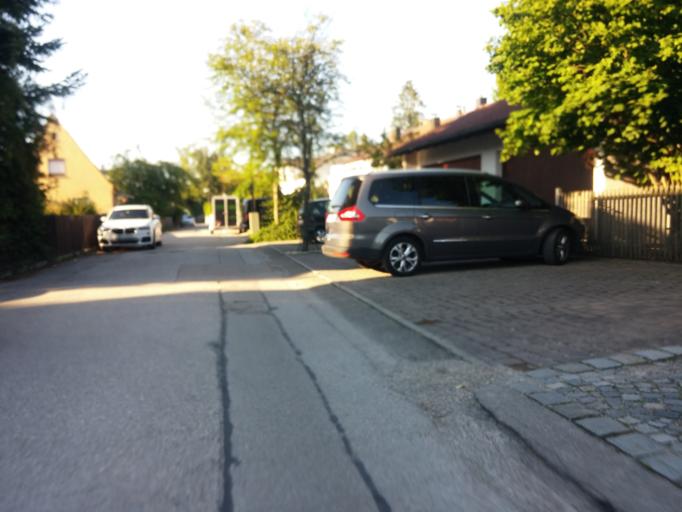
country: DE
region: Bavaria
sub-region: Upper Bavaria
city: Vaterstetten
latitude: 48.1029
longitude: 11.7947
